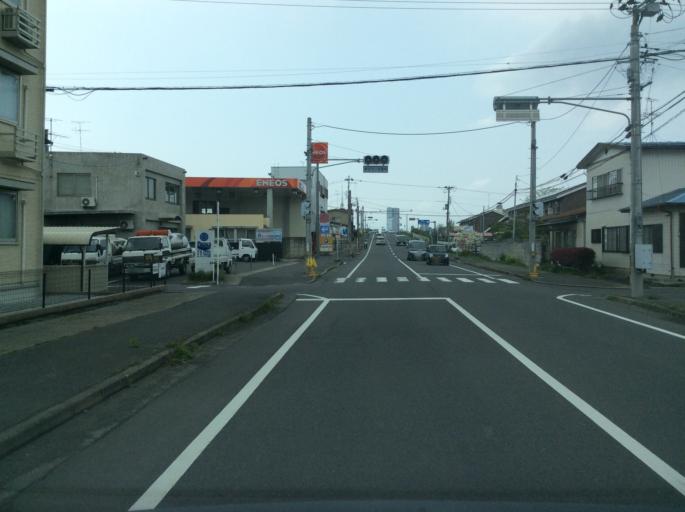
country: JP
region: Fukushima
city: Koriyama
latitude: 37.3843
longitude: 140.4038
